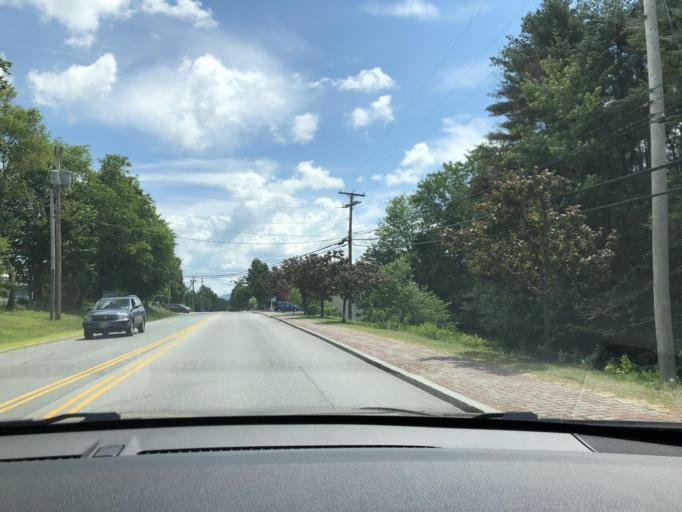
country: US
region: New Hampshire
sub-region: Merrimack County
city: New London
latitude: 43.4223
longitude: -71.9983
